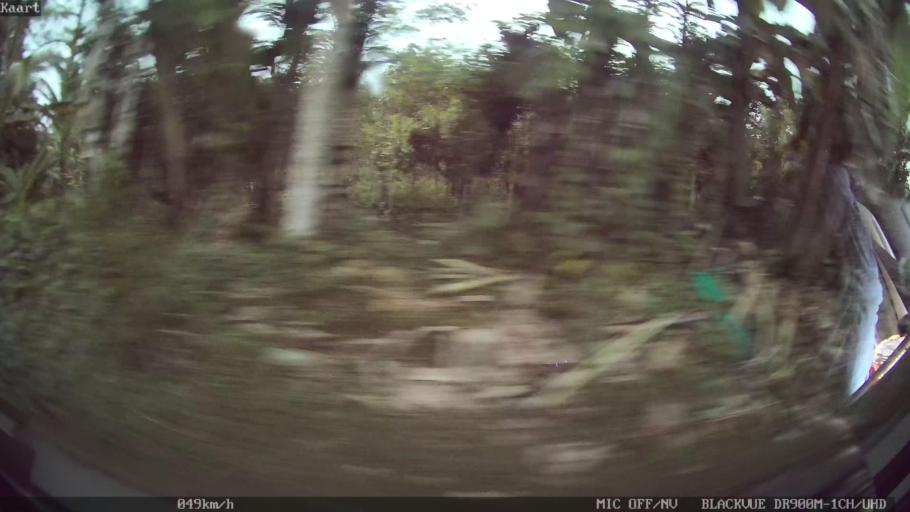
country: ID
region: Bali
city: Peneng
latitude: -8.3420
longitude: 115.2111
